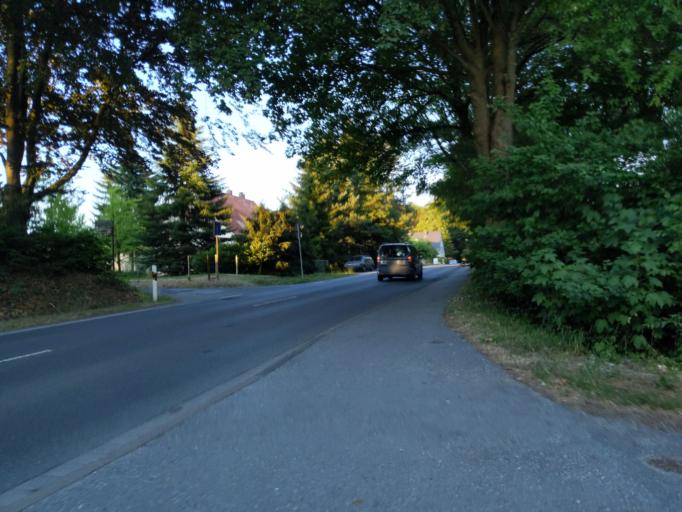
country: DE
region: North Rhine-Westphalia
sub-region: Regierungsbezirk Detmold
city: Bielefeld
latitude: 52.0220
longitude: 8.4919
